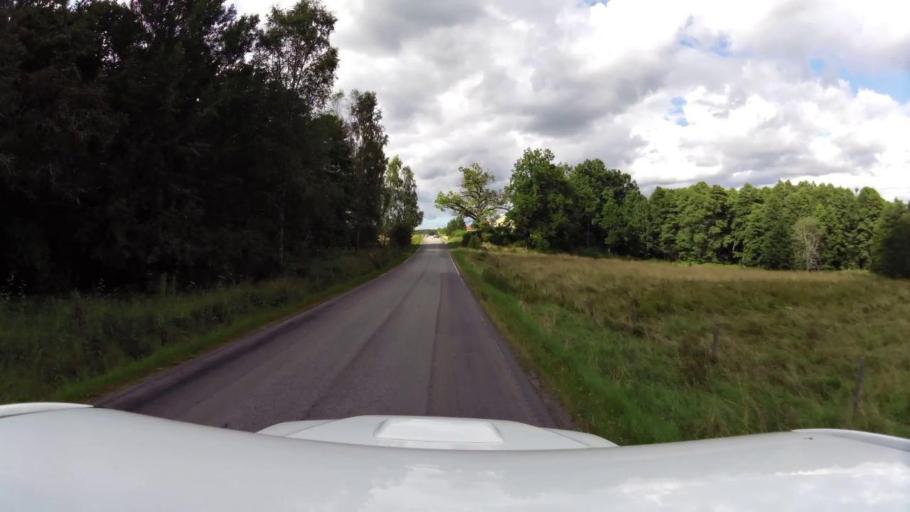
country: SE
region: OEstergoetland
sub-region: Linkopings Kommun
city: Sturefors
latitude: 58.3237
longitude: 15.7169
